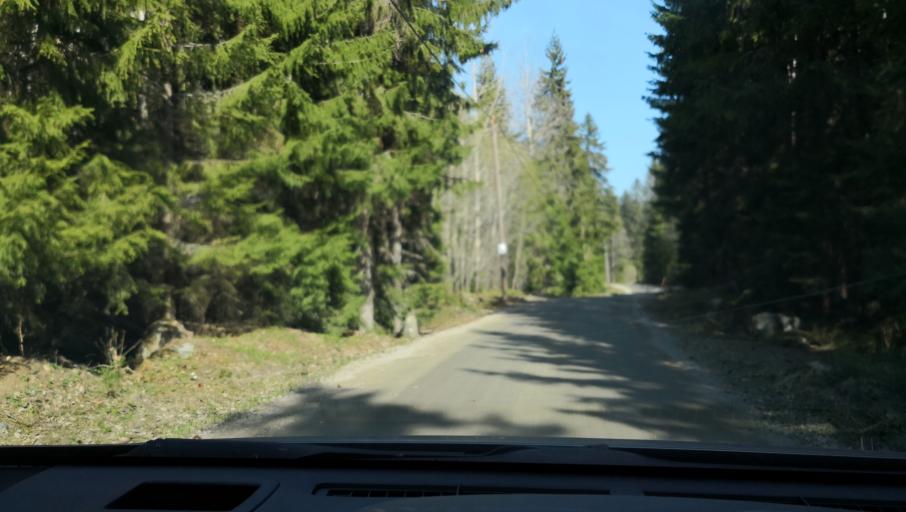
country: SE
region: Uppsala
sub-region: Heby Kommun
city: Heby
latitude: 60.0137
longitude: 16.7387
